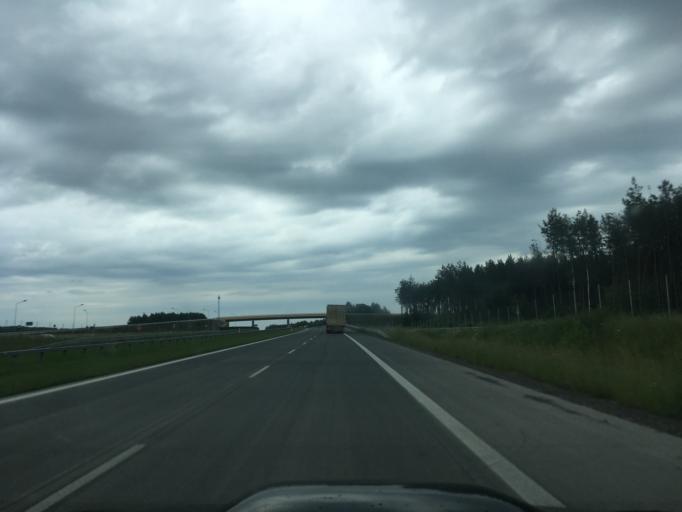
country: PL
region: Masovian Voivodeship
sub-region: Powiat garwolinski
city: Pilawa
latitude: 51.9867
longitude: 21.5512
